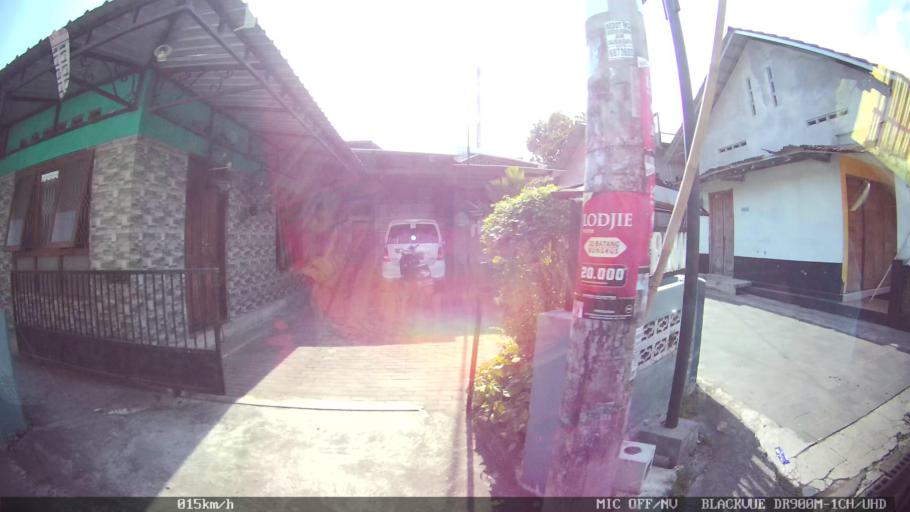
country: ID
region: Daerah Istimewa Yogyakarta
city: Sewon
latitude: -7.8319
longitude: 110.4020
